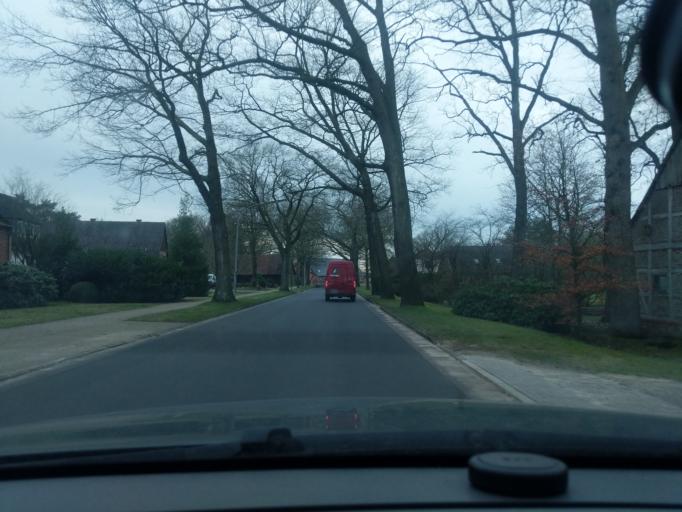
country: DE
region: Lower Saxony
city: Helvesiek
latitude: 53.2166
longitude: 9.4880
